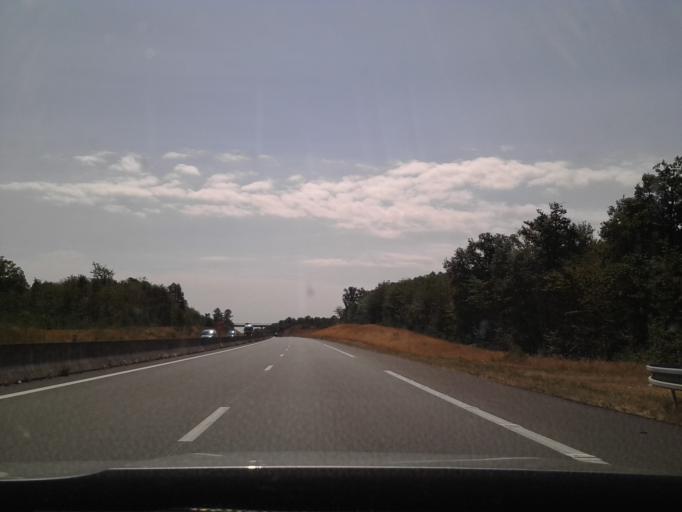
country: FR
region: Pays de la Loire
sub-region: Departement de la Sarthe
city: Mayet
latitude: 47.7359
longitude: 0.3245
